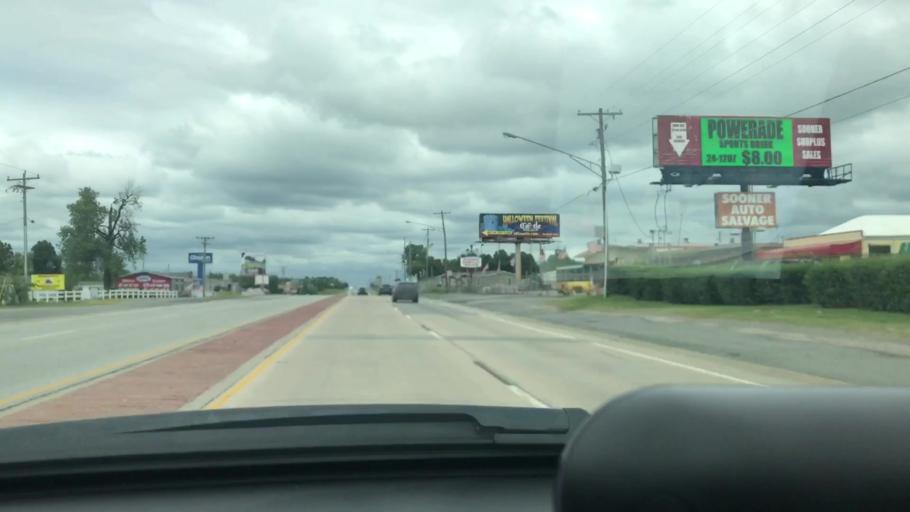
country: US
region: Oklahoma
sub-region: Muskogee County
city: Muskogee
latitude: 35.7737
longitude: -95.4025
